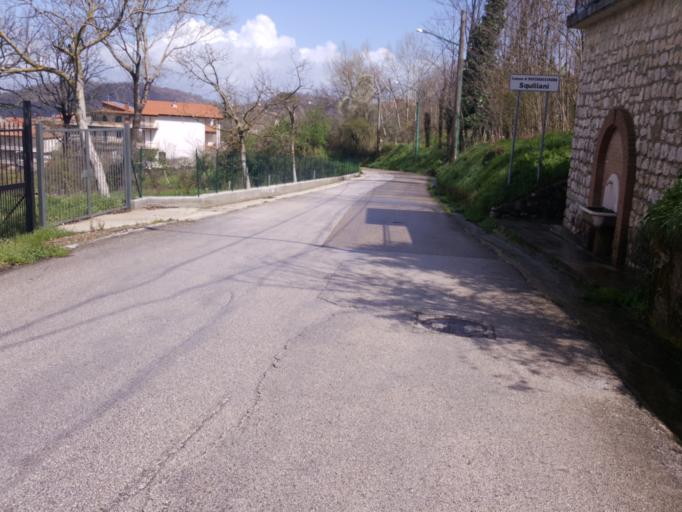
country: IT
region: Campania
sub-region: Provincia di Avellino
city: Roccabascerana
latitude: 41.0408
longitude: 14.7168
